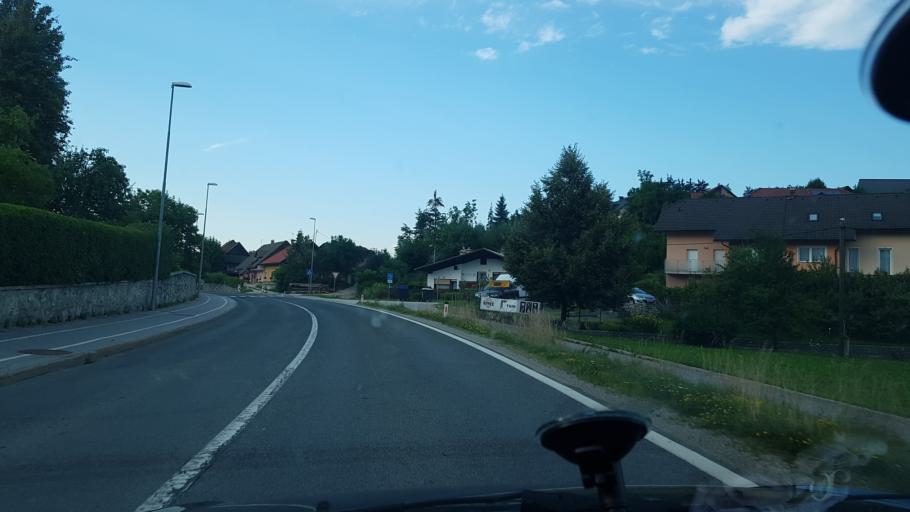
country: SI
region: Logatec
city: Logatec
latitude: 45.8992
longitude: 14.2006
